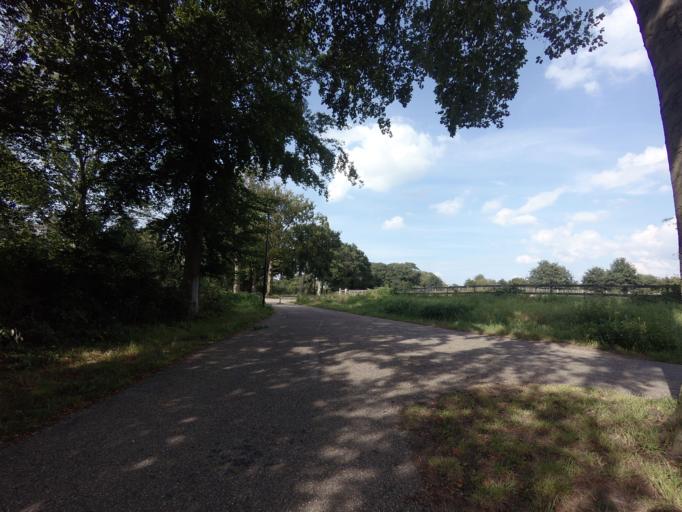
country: NL
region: Overijssel
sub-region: Gemeente Deventer
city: Schalkhaar
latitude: 52.2558
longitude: 6.2122
